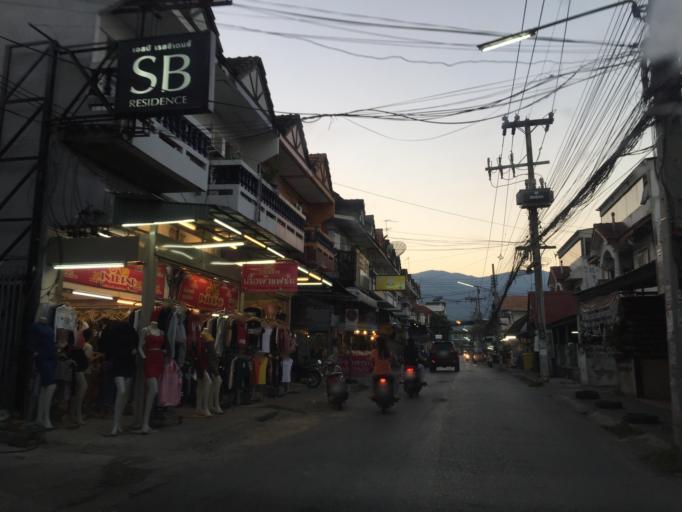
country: TH
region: Chiang Mai
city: Chiang Mai
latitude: 18.8044
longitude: 98.9820
